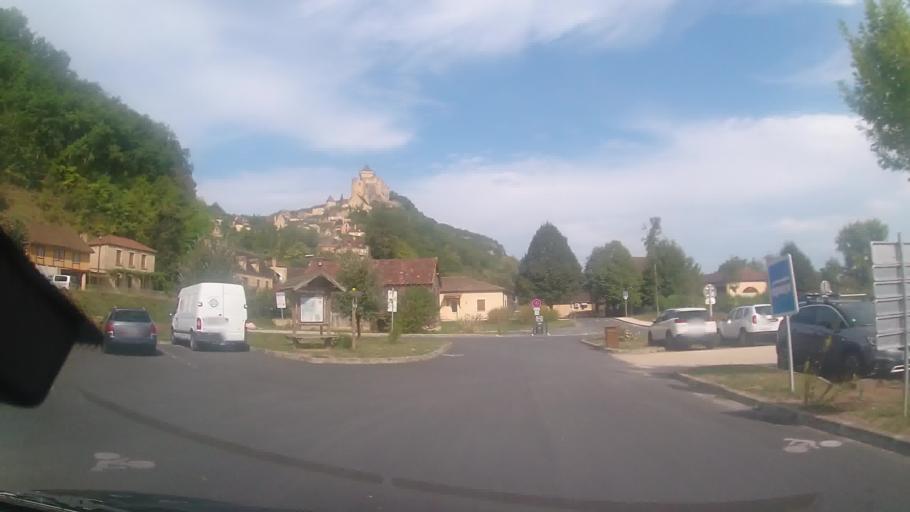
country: FR
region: Aquitaine
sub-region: Departement de la Dordogne
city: Cenac-et-Saint-Julien
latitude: 44.8128
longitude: 1.1526
